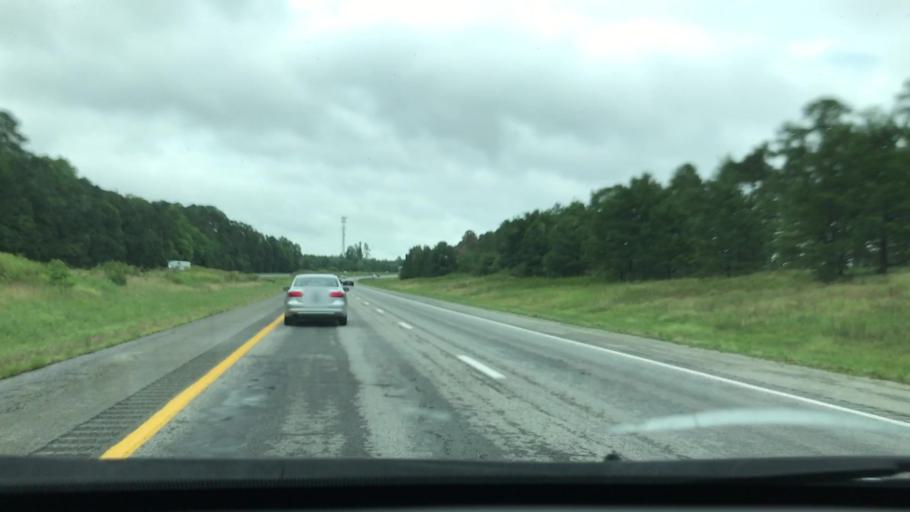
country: US
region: Virginia
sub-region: City of Emporia
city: Emporia
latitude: 36.8207
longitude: -77.4548
